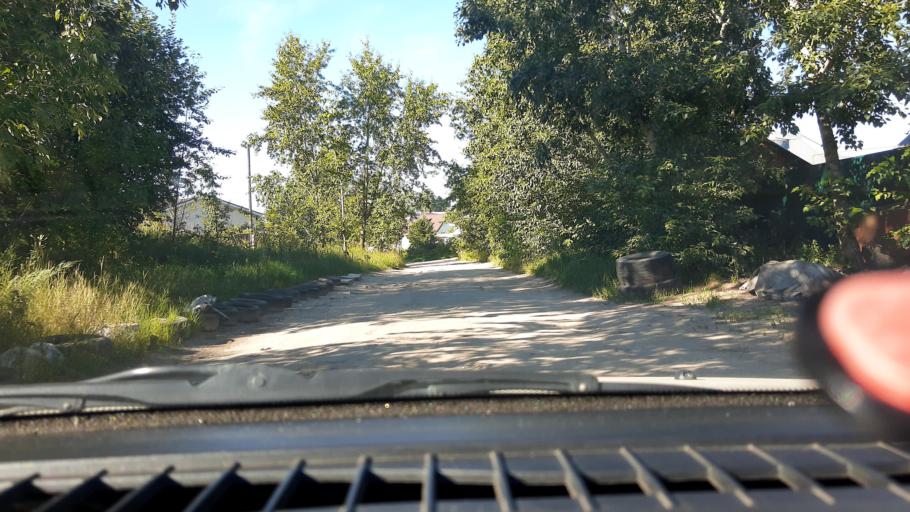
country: RU
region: Nizjnij Novgorod
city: Gorbatovka
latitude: 56.3776
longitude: 43.7992
